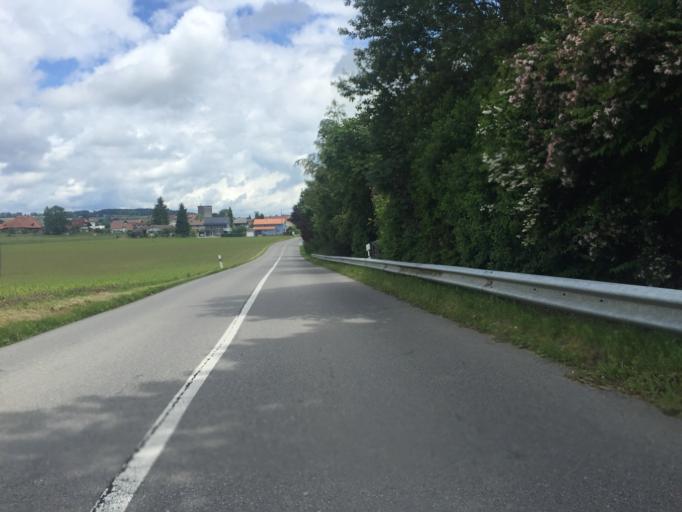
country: CH
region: Bern
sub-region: Bern-Mittelland District
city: Wohlen
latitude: 46.9839
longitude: 7.3790
